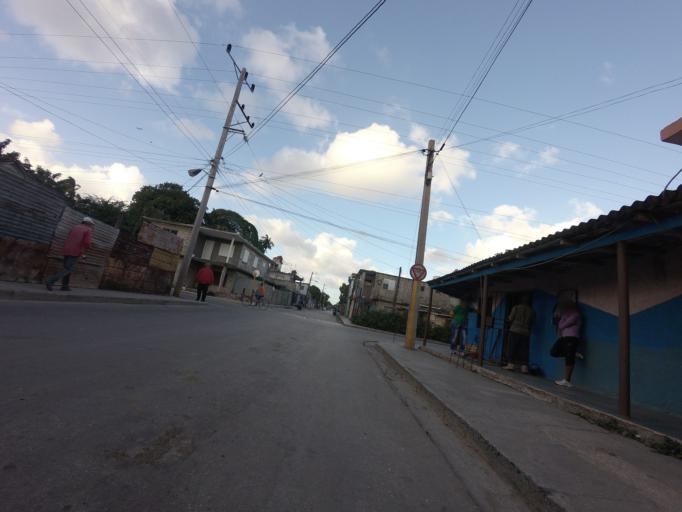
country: CU
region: Ciego de Avila
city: Ciego de Avila
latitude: 21.8337
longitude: -78.7570
